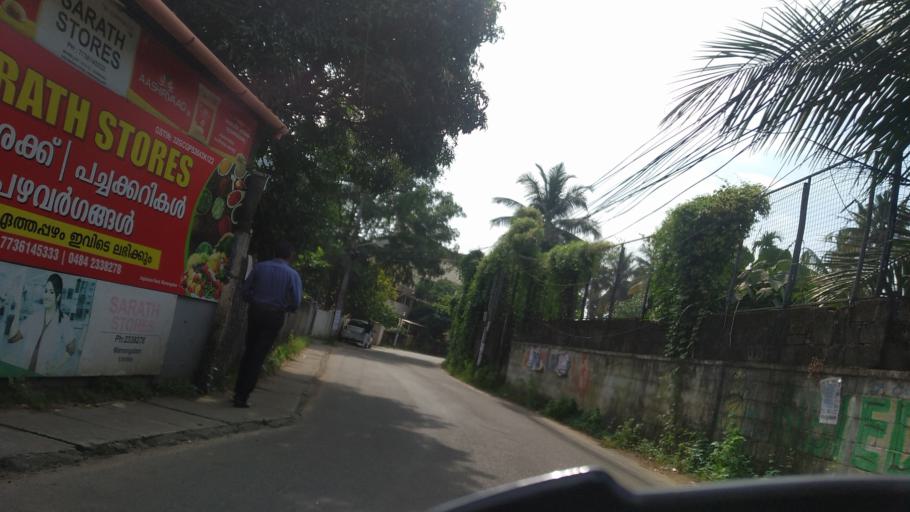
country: IN
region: Kerala
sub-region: Ernakulam
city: Elur
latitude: 10.0101
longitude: 76.3054
